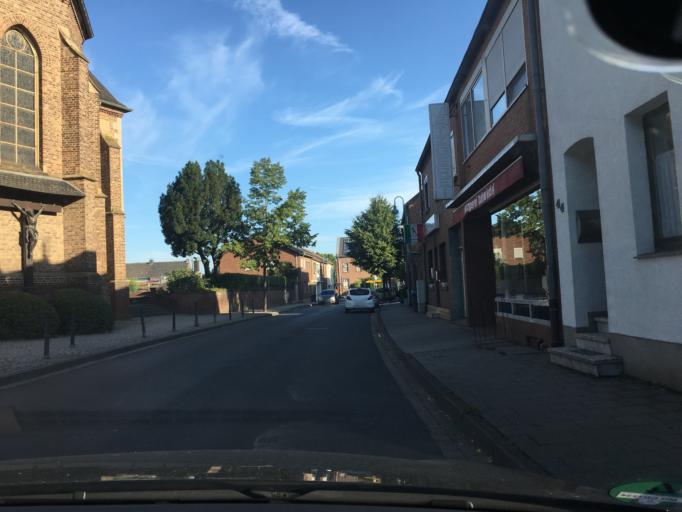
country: DE
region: North Rhine-Westphalia
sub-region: Regierungsbezirk Koln
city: Niederzier
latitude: 50.8854
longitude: 6.4634
